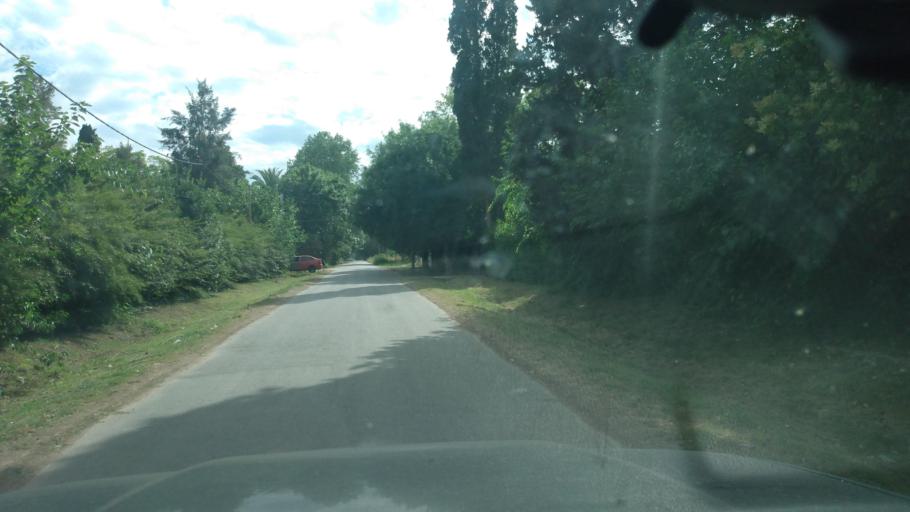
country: AR
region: Buenos Aires
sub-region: Partido de Lujan
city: Lujan
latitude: -34.5907
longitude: -59.0542
